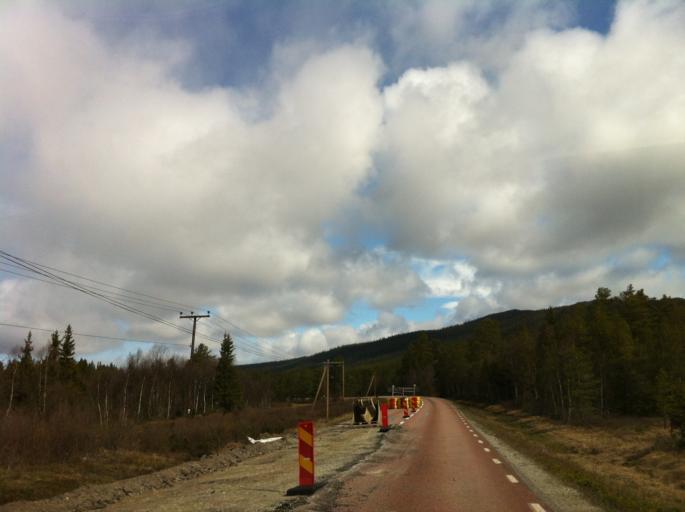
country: SE
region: Jaemtland
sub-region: Are Kommun
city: Are
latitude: 62.5540
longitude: 12.5670
